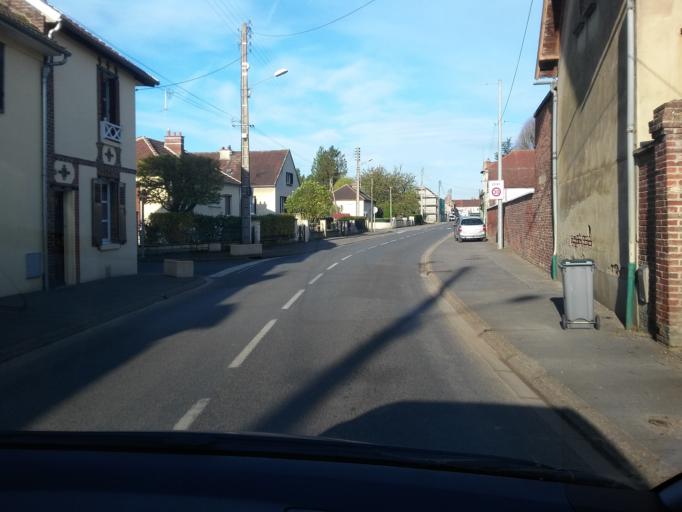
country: FR
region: Picardie
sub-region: Departement de l'Oise
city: Chevrieres
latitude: 49.3472
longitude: 2.6859
